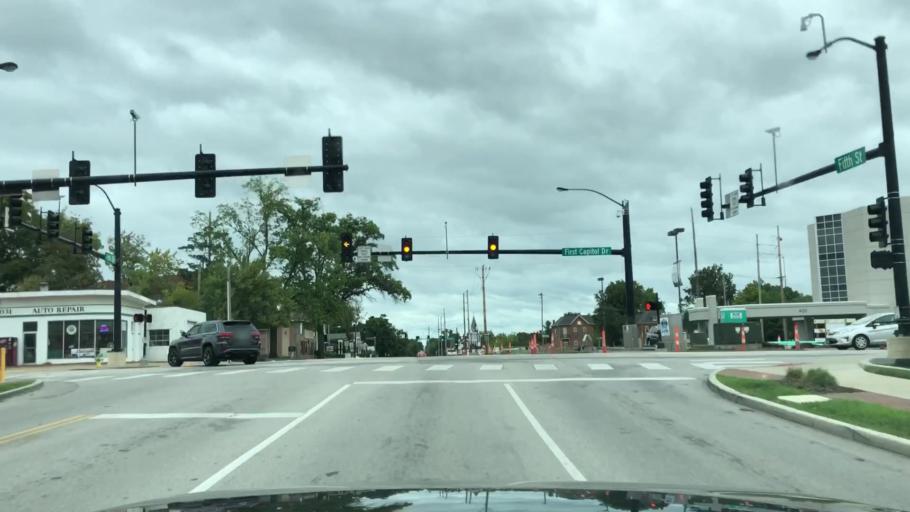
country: US
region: Missouri
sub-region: Saint Charles County
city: Saint Charles
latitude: 38.7799
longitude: -90.4855
